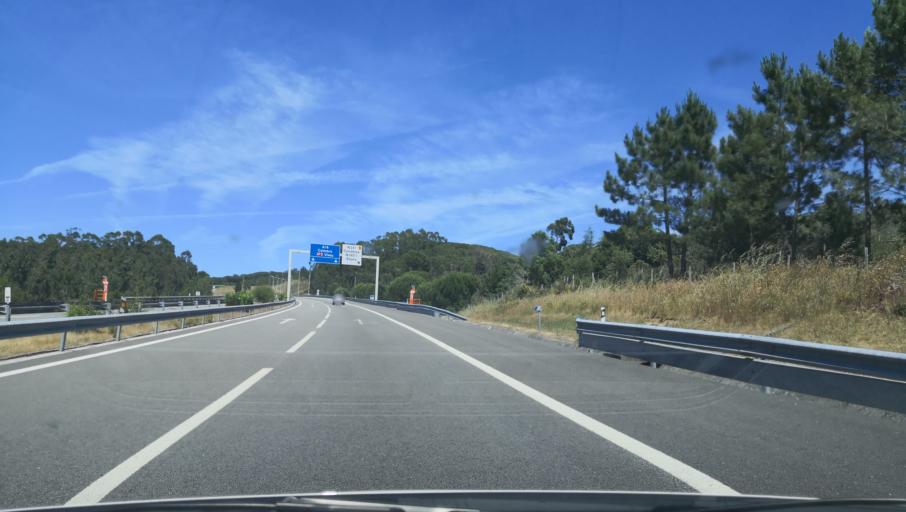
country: PT
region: Coimbra
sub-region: Montemor-O-Velho
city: Montemor-o-Velho
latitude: 40.1977
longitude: -8.6803
